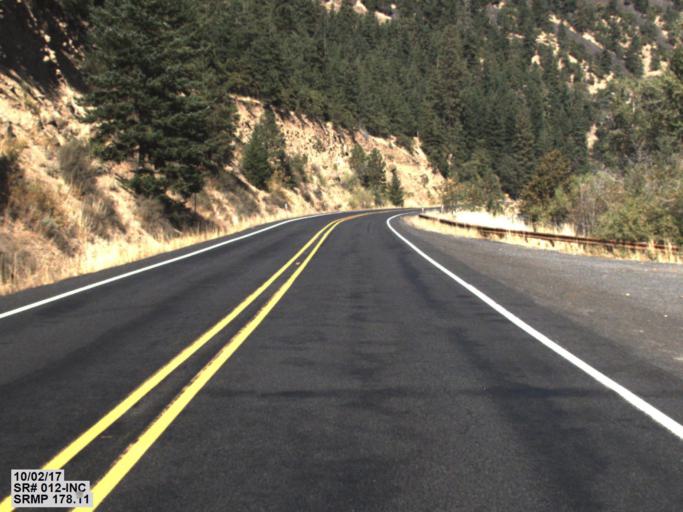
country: US
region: Washington
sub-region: Yakima County
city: Tieton
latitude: 46.6991
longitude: -120.8989
